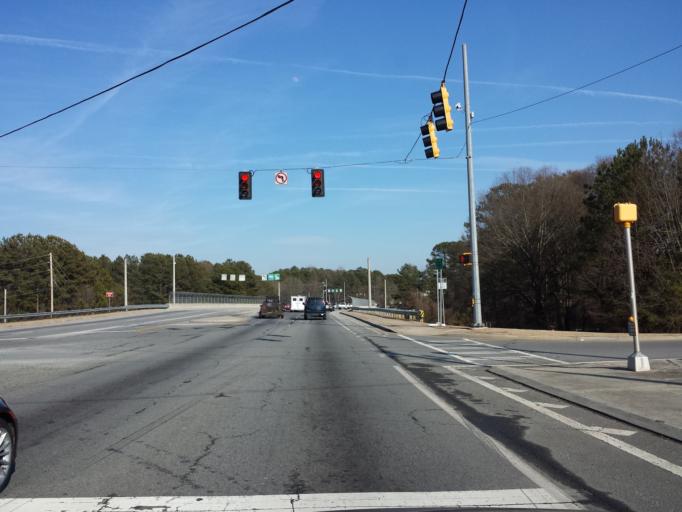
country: US
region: Georgia
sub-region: Cobb County
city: Kennesaw
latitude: 34.0376
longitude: -84.5642
